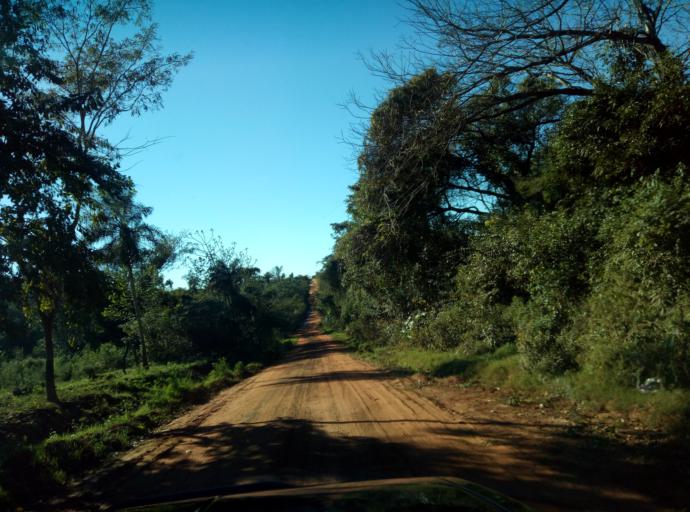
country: PY
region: Caaguazu
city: Doctor Cecilio Baez
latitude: -25.1587
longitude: -56.2908
